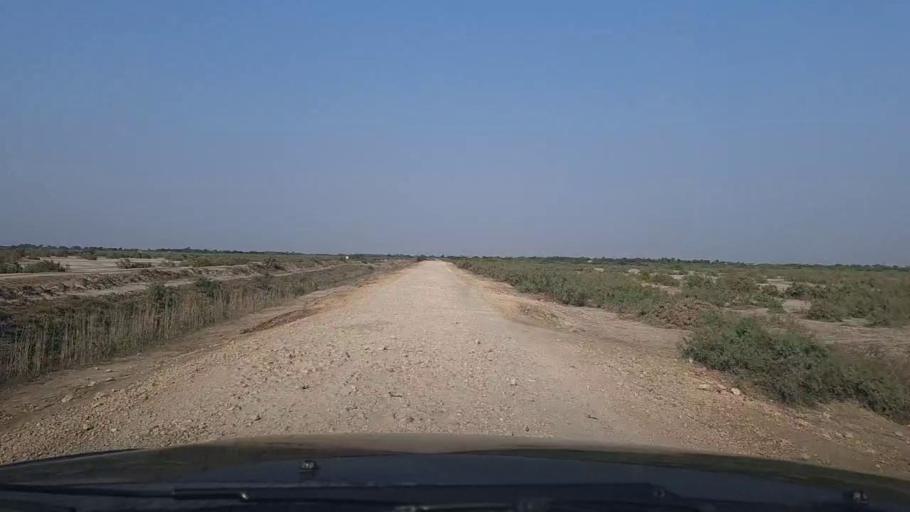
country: PK
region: Sindh
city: Mirpur Sakro
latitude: 24.6468
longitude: 67.7543
